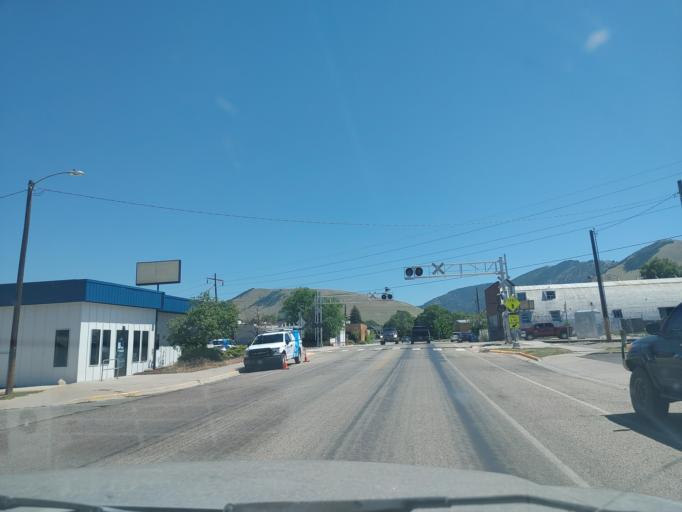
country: US
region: Montana
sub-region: Missoula County
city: Missoula
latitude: 46.8670
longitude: -114.0115
